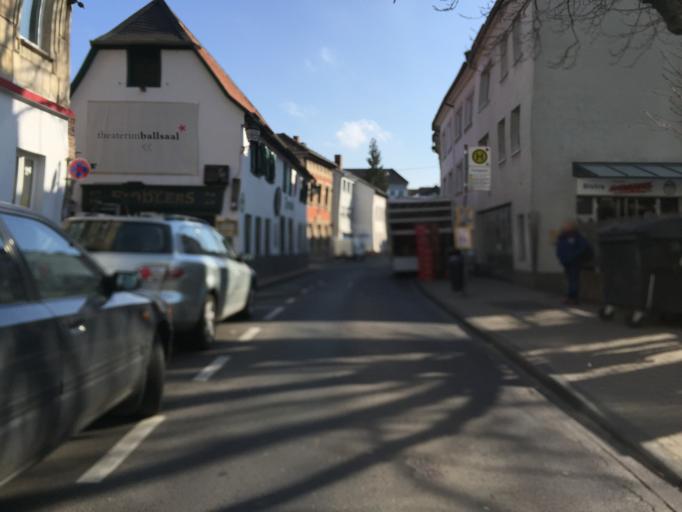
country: DE
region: North Rhine-Westphalia
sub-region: Regierungsbezirk Koln
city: Bonn
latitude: 50.7276
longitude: 7.0742
